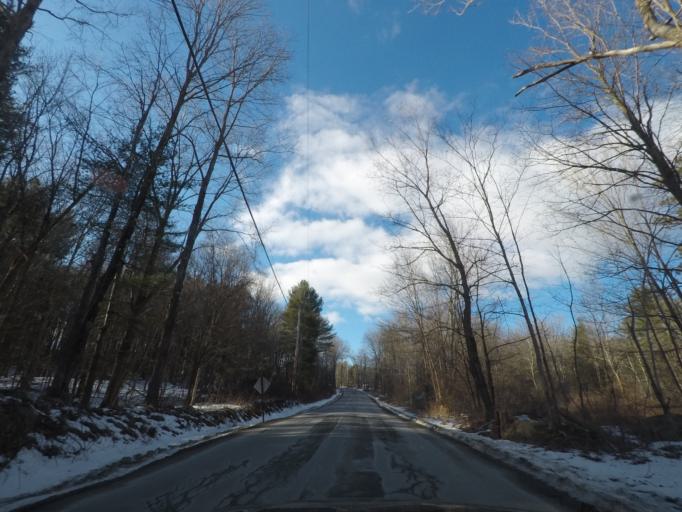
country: US
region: New York
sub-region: Rensselaer County
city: Nassau
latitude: 42.5172
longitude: -73.5201
